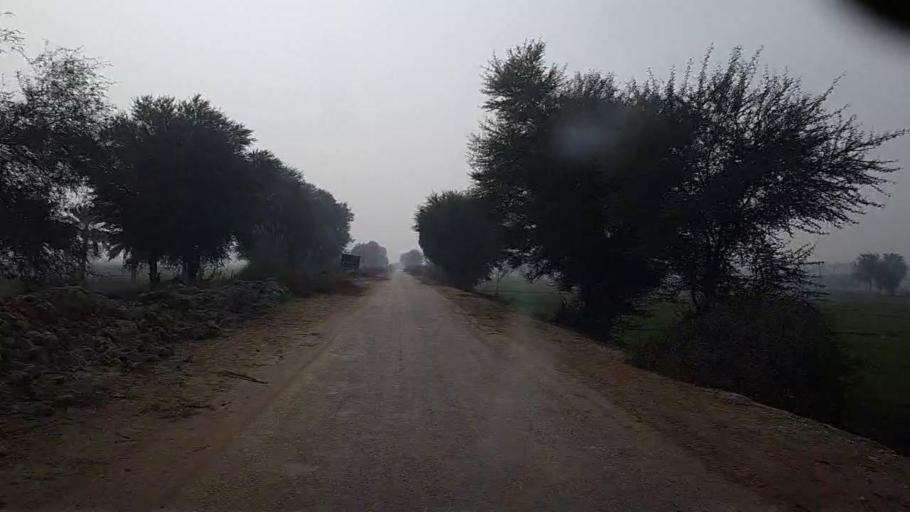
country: PK
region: Sindh
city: Kandiari
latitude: 26.9870
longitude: 68.6036
